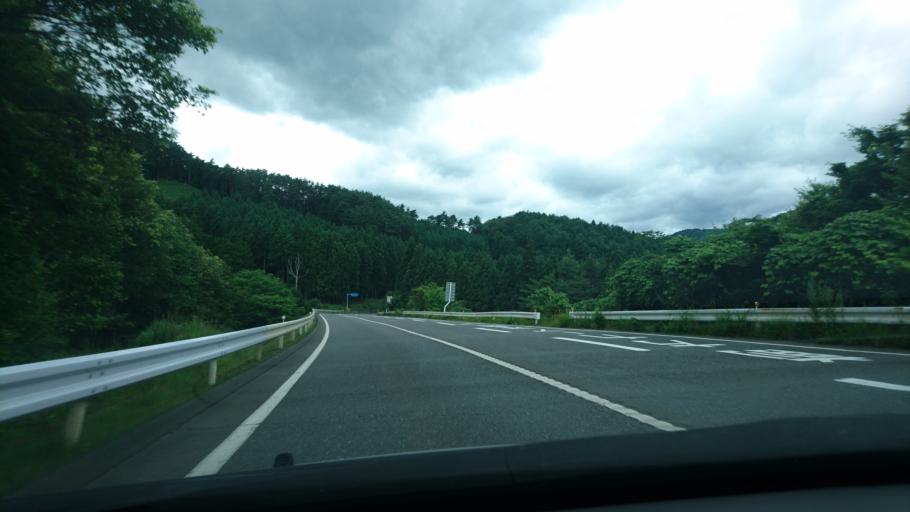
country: JP
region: Iwate
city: Kamaishi
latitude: 39.1856
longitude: 141.8518
